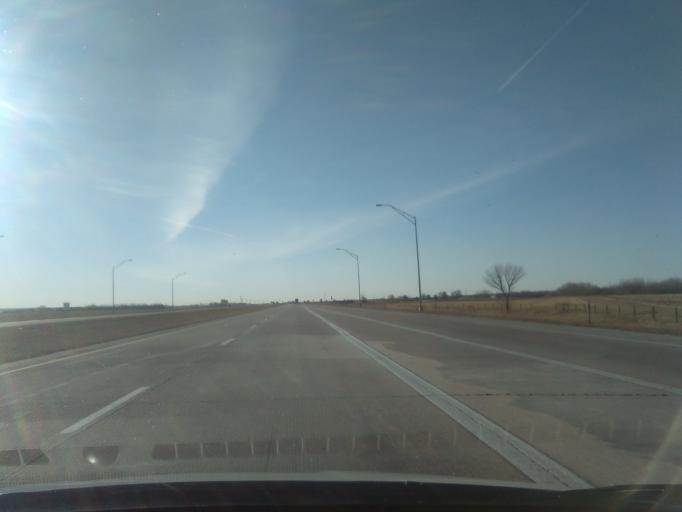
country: US
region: Colorado
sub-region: Sedgwick County
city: Julesburg
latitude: 41.0475
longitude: -102.0757
